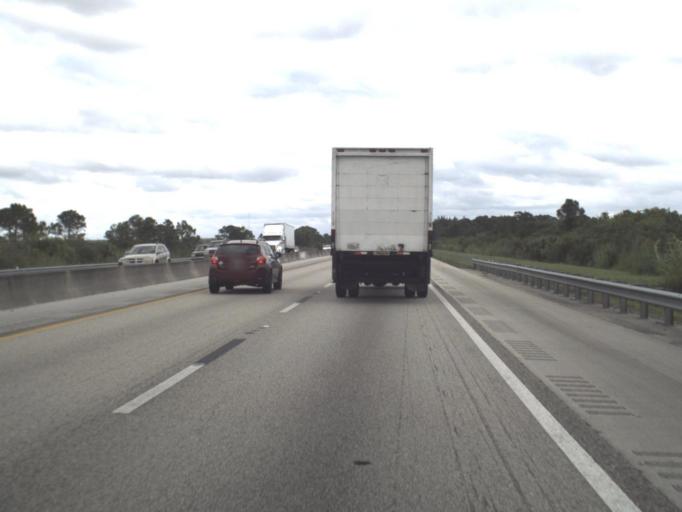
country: US
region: Florida
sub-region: Palm Beach County
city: Tequesta
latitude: 27.0071
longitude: -80.2106
